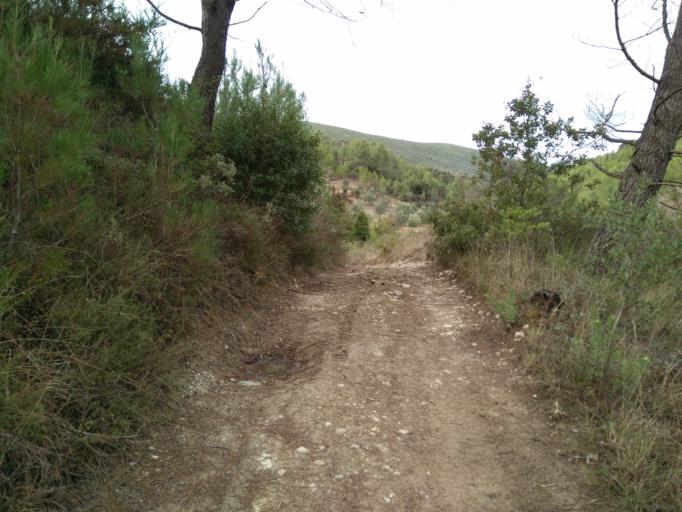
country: PT
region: Leiria
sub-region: Porto de Mos
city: Porto de Mos
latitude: 39.5792
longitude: -8.8144
